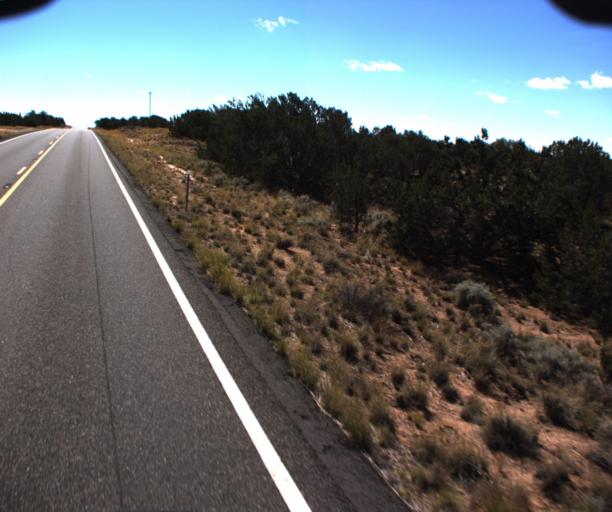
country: US
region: Arizona
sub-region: Apache County
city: Saint Johns
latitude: 34.8509
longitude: -109.2377
